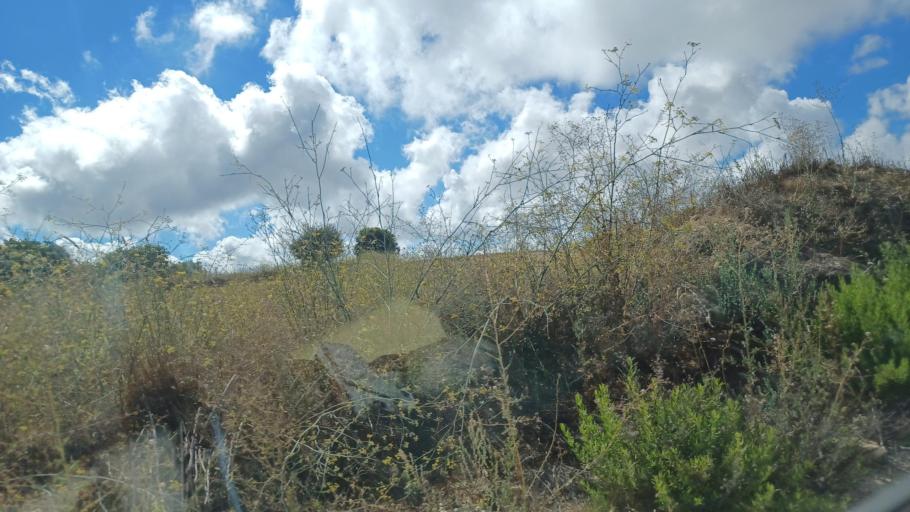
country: CY
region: Pafos
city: Tala
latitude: 34.8565
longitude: 32.4478
